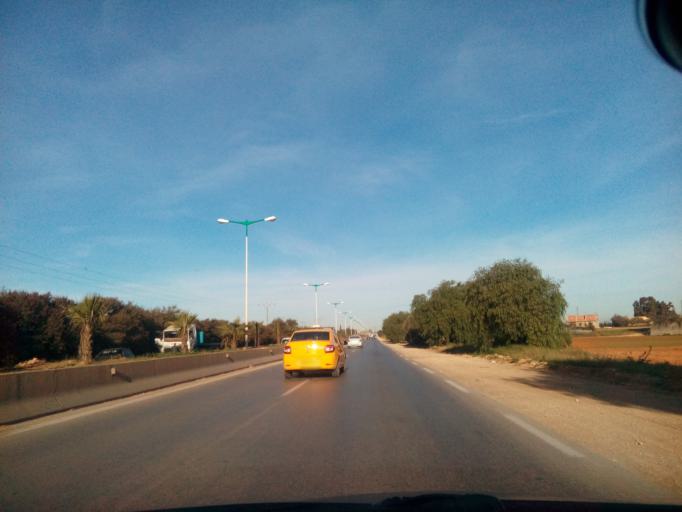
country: DZ
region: Mostaganem
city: Mostaganem
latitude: 35.8612
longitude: 0.1590
